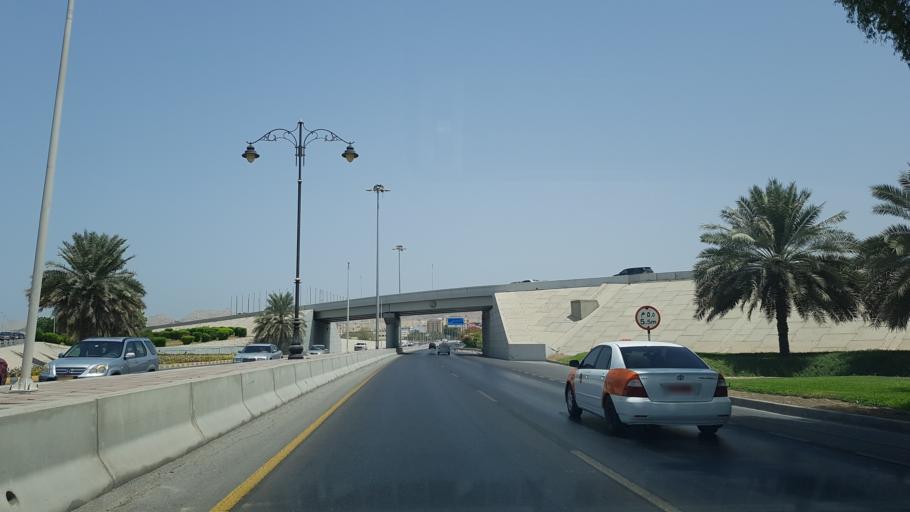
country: OM
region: Muhafazat Masqat
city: Bawshar
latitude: 23.6143
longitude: 58.4845
